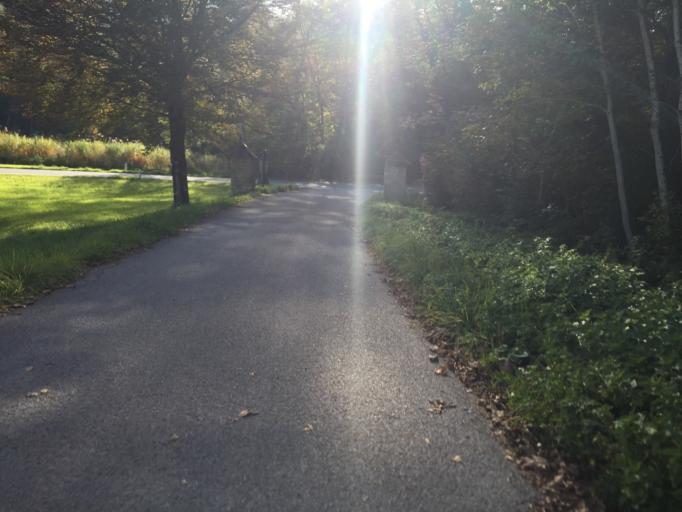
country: AT
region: Salzburg
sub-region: Politischer Bezirk Salzburg-Umgebung
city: Grodig
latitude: 47.7478
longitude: 13.0037
